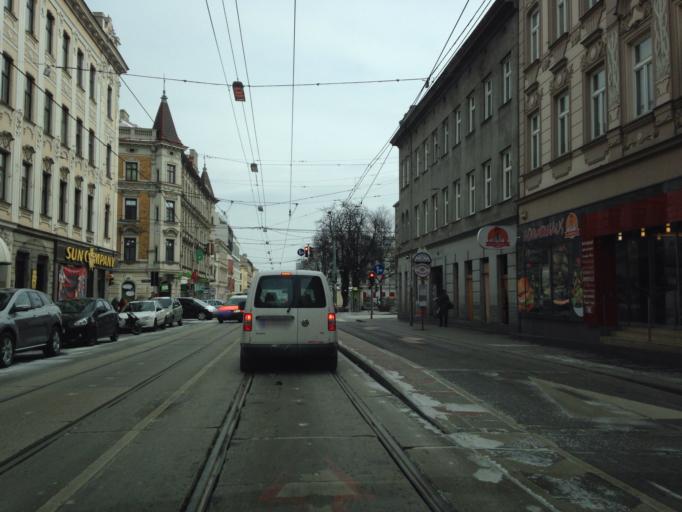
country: AT
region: Vienna
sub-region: Wien Stadt
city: Vienna
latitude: 48.2117
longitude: 16.3182
